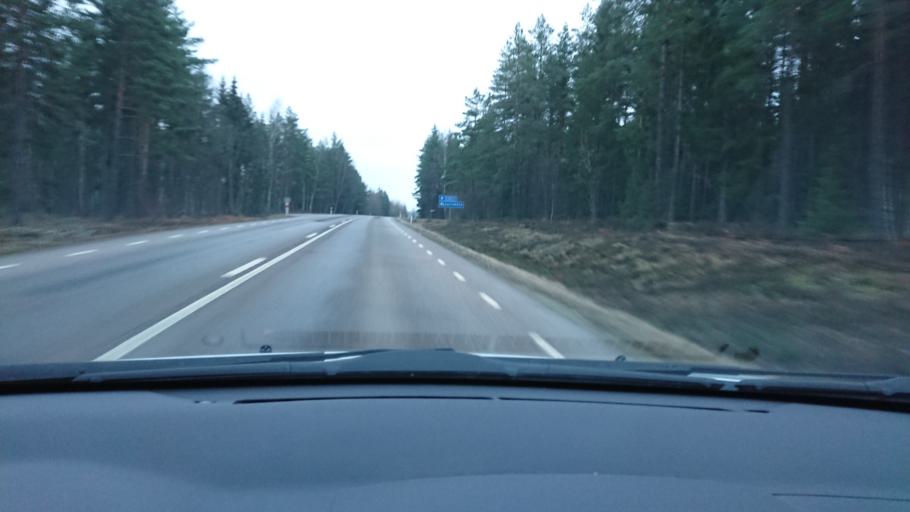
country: SE
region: Kronoberg
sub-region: Vaxjo Kommun
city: Braas
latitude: 57.0790
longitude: 15.1718
